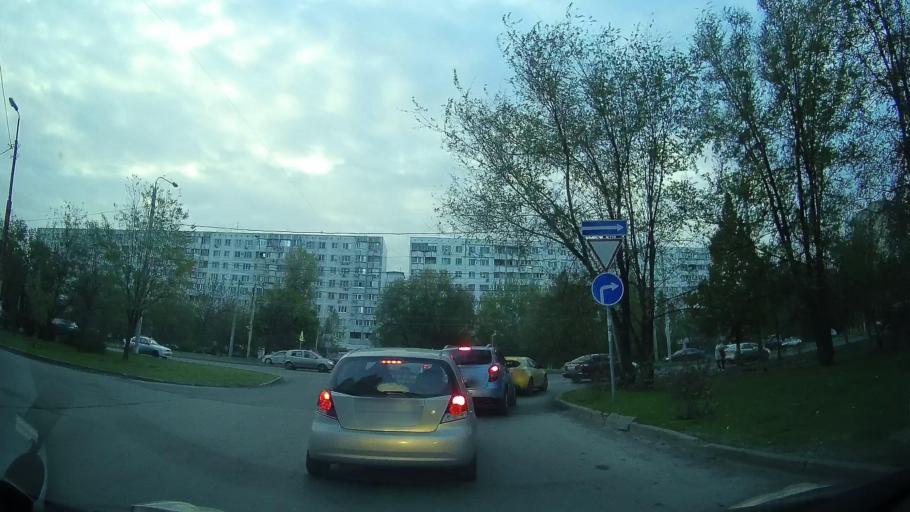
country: RU
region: Rostov
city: Severnyy
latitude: 47.2581
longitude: 39.6446
